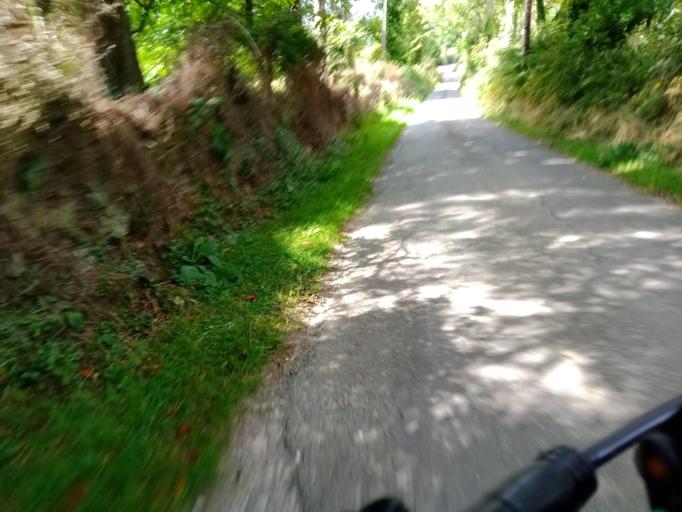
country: IE
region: Munster
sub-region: Waterford
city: Dungarvan
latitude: 52.1366
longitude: -7.4756
